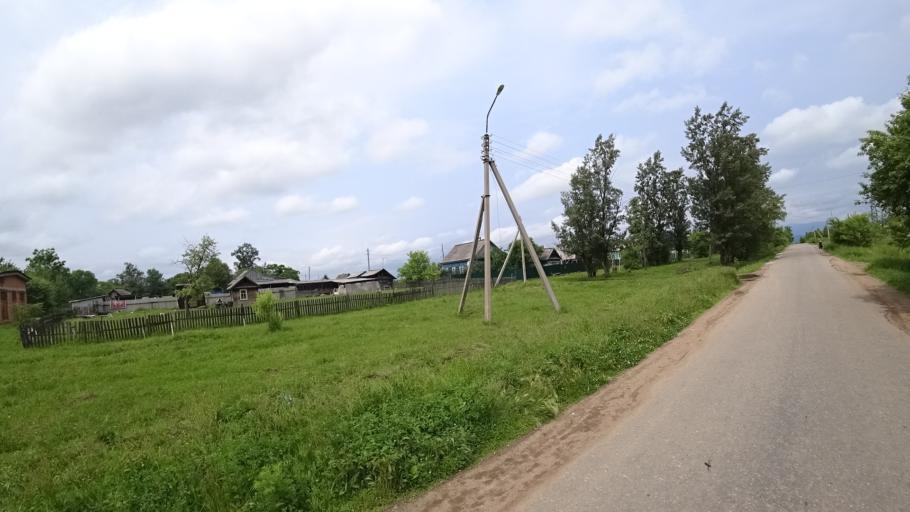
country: RU
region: Primorskiy
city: Novosysoyevka
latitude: 44.2308
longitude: 133.3606
